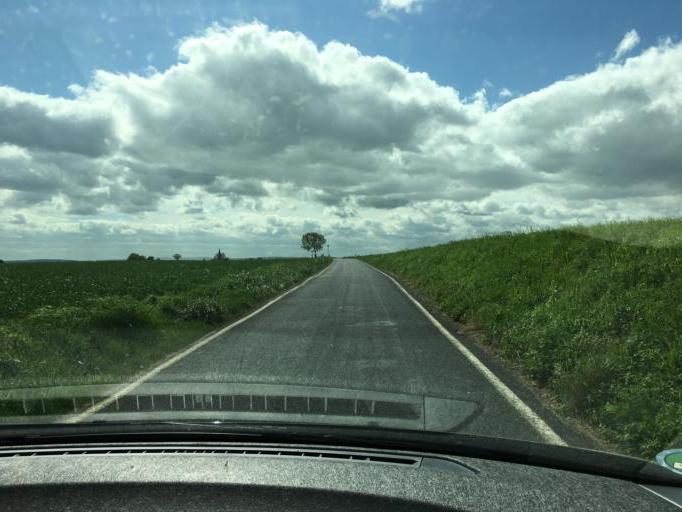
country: DE
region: North Rhine-Westphalia
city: Zulpich
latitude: 50.6847
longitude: 6.6078
